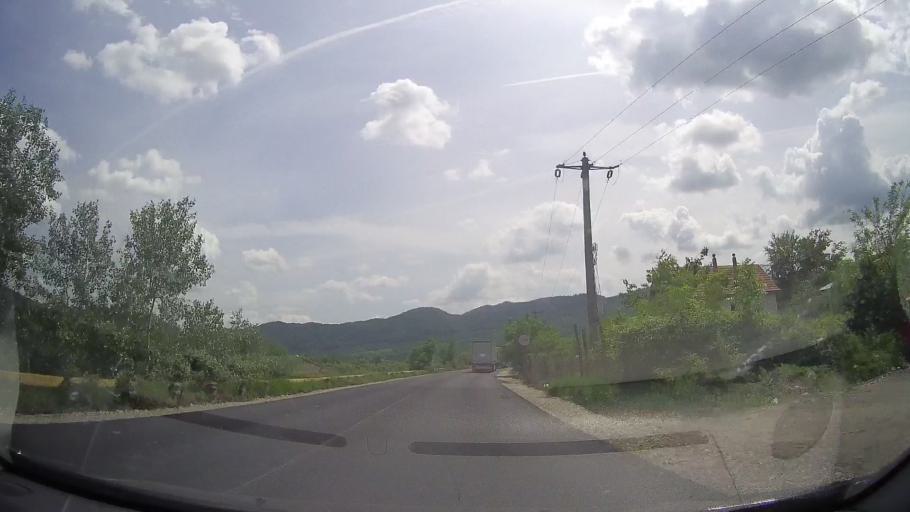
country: RO
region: Valcea
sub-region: Oras Calimanesti
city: Jiblea Veche
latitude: 45.2373
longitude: 24.3452
